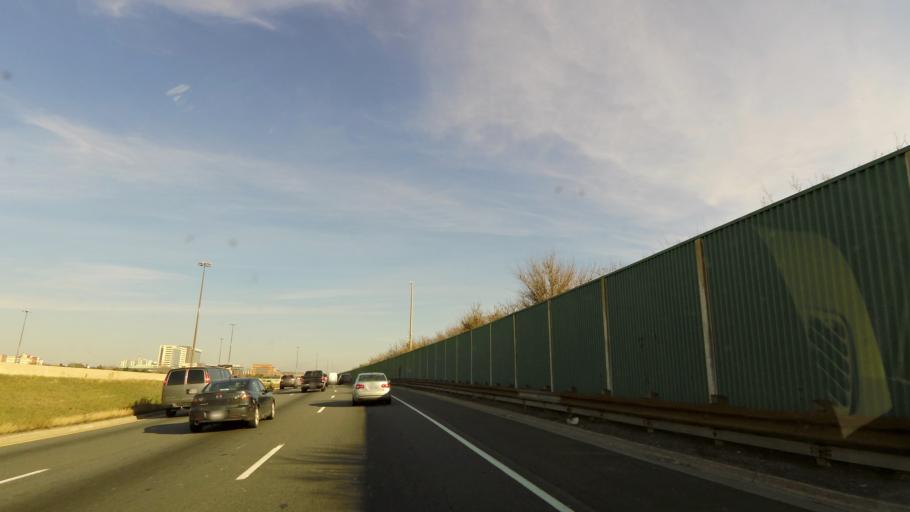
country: CA
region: Ontario
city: Concord
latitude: 43.7175
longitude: -79.5008
